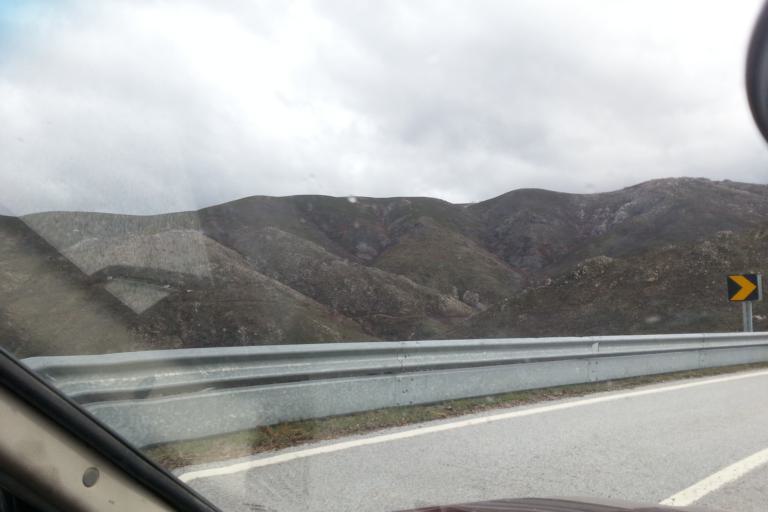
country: PT
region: Guarda
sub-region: Manteigas
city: Manteigas
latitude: 40.4560
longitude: -7.5942
